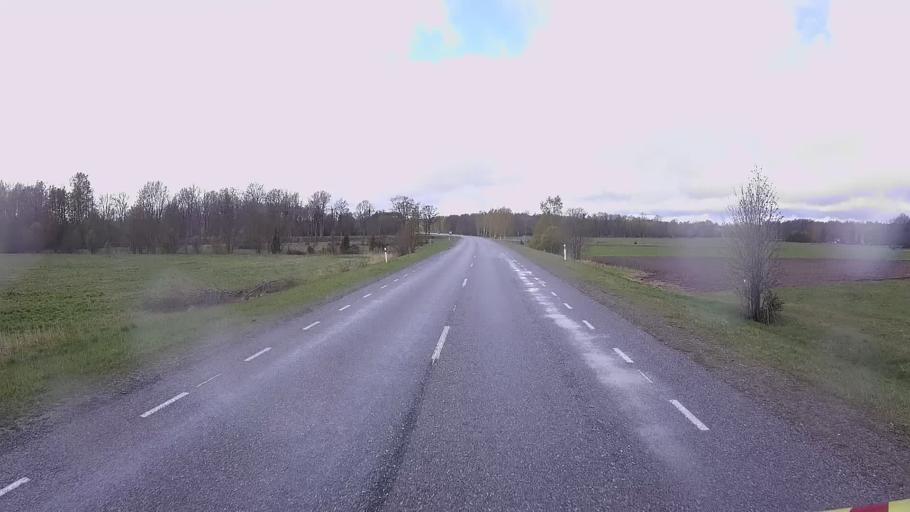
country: EE
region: Hiiumaa
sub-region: Kaerdla linn
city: Kardla
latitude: 58.8269
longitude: 22.7557
